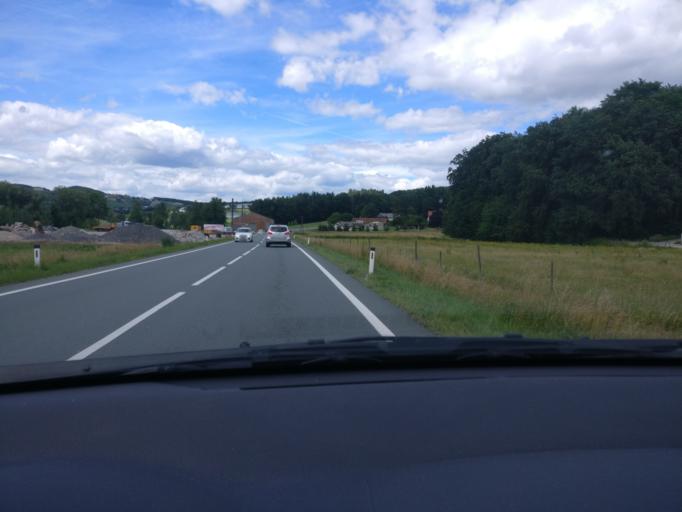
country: AT
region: Styria
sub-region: Politischer Bezirk Weiz
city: Hirnsdorf
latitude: 47.1781
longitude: 15.8101
